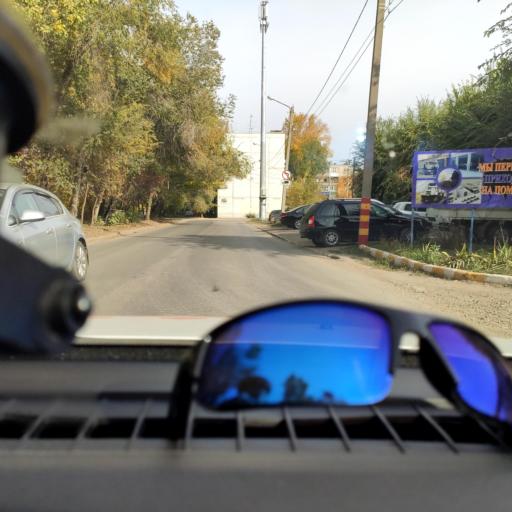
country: RU
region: Samara
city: Samara
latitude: 53.1194
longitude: 50.0923
